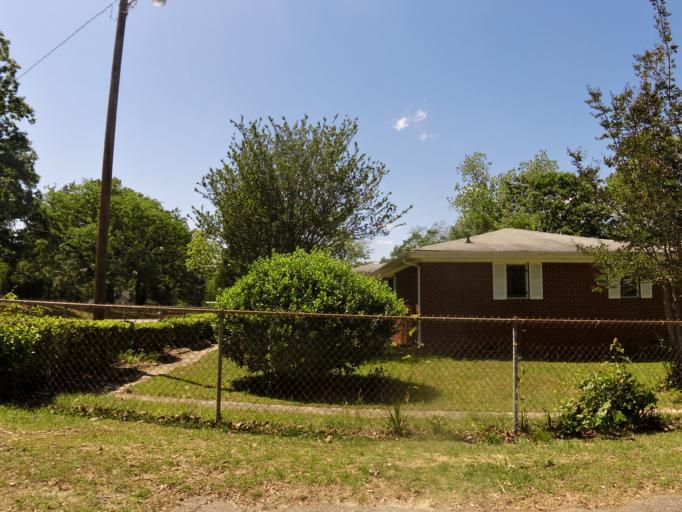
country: US
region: South Carolina
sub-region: Aiken County
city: Aiken
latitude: 33.5653
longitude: -81.7125
